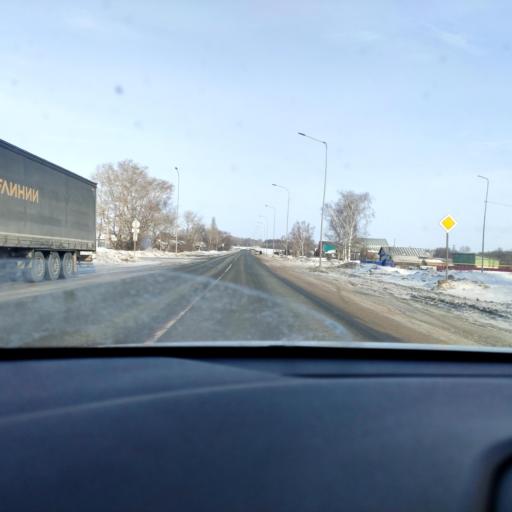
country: RU
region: Tatarstan
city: Buinsk
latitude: 54.8818
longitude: 48.2650
